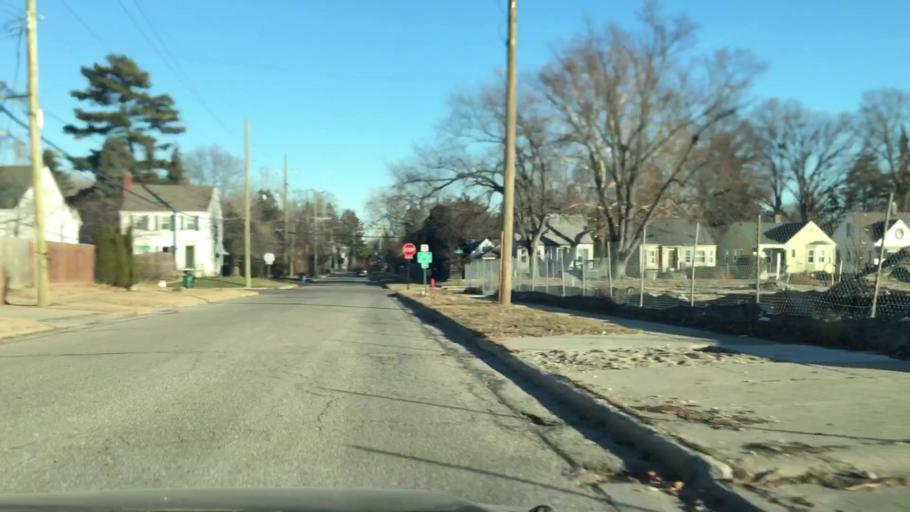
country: US
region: Michigan
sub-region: Oakland County
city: Ferndale
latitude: 42.4495
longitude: -83.1384
